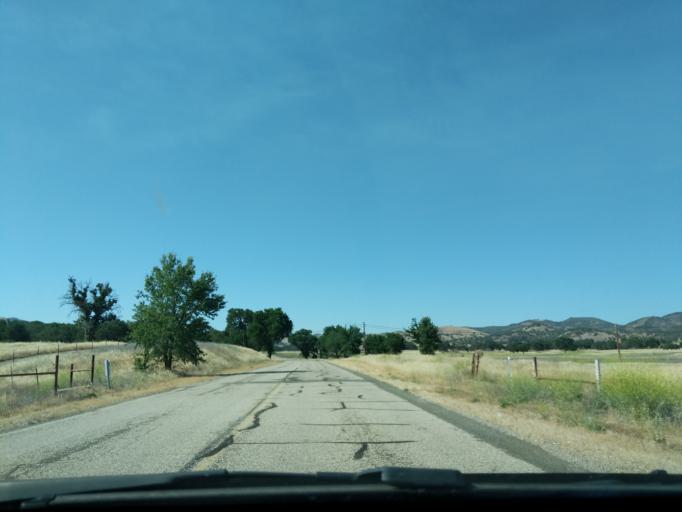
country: US
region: California
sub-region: Monterey County
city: King City
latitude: 36.0216
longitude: -121.1779
